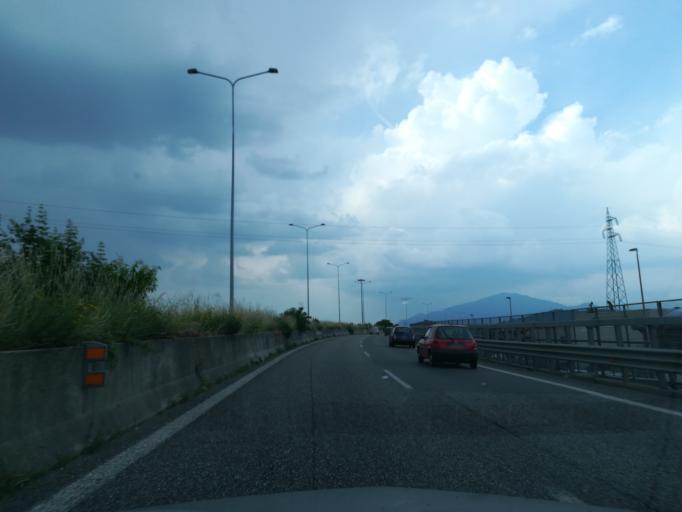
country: IT
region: Lombardy
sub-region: Provincia di Bergamo
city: Lallio
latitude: 45.6779
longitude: 9.6401
